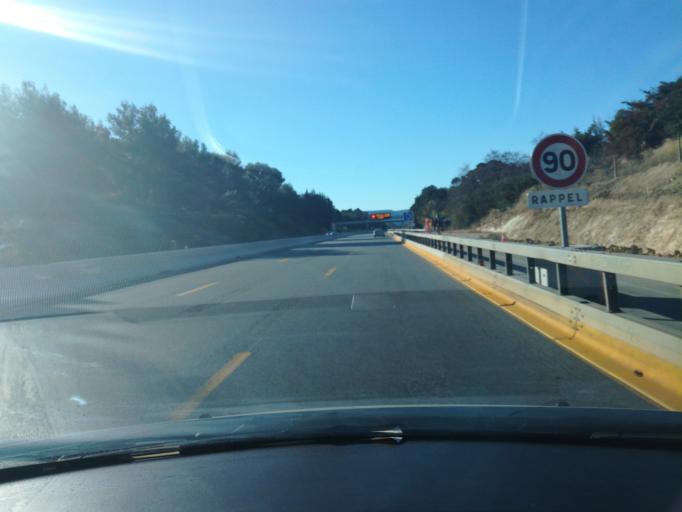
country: FR
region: Provence-Alpes-Cote d'Azur
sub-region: Departement des Bouches-du-Rhone
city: Roquevaire
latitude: 43.3367
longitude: 5.6070
